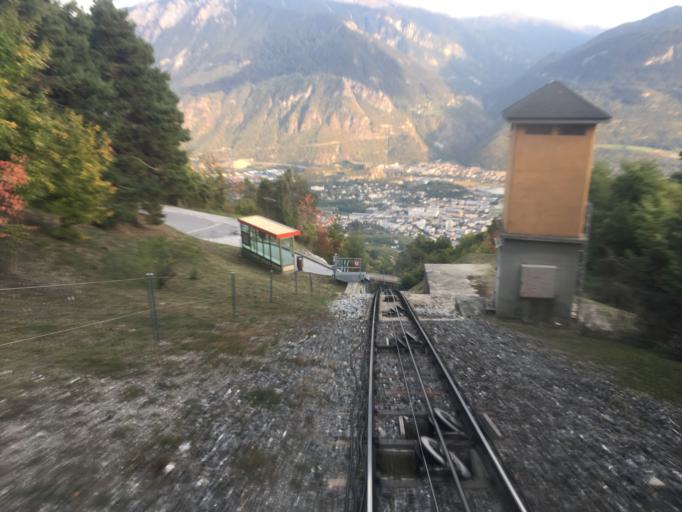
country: CH
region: Valais
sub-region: Sierre District
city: Randogne
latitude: 46.3060
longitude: 7.5082
